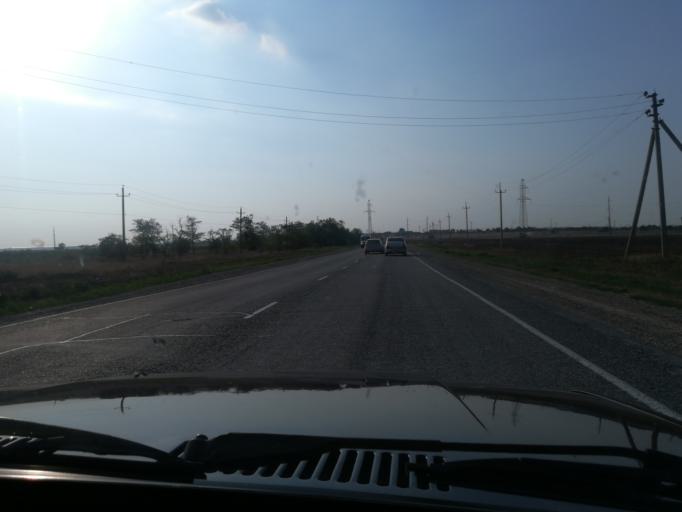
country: RU
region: Krasnodarskiy
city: Yurovka
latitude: 45.1020
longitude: 37.4262
